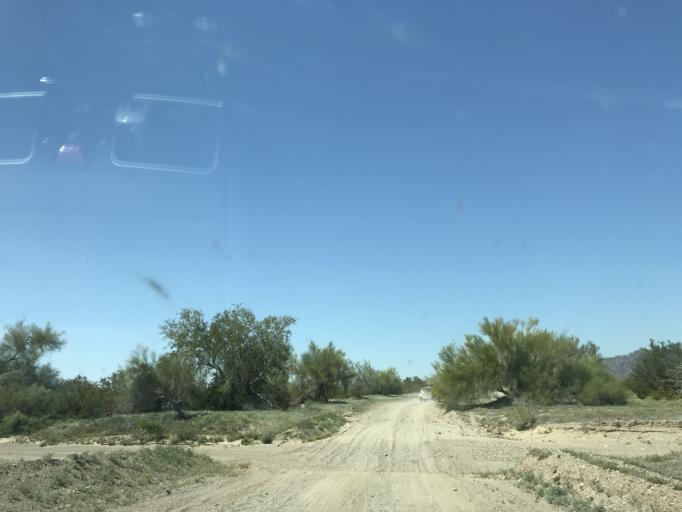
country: US
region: California
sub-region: Riverside County
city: Mesa Verde
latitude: 33.4895
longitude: -114.8935
